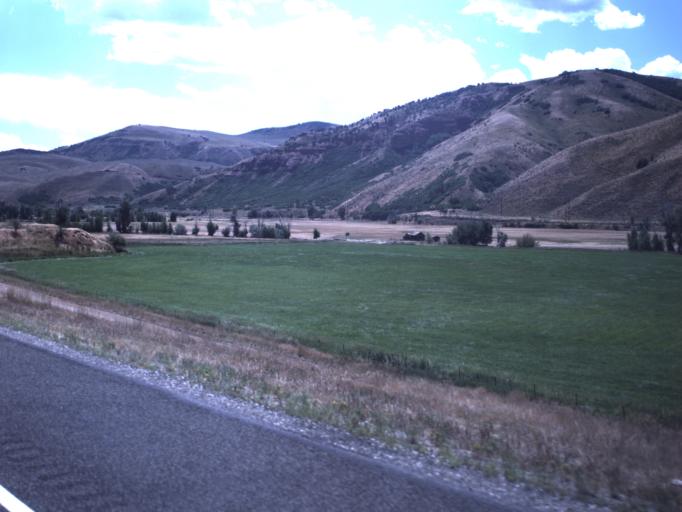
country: US
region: Utah
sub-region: Summit County
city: Coalville
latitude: 40.9877
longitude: -111.4531
